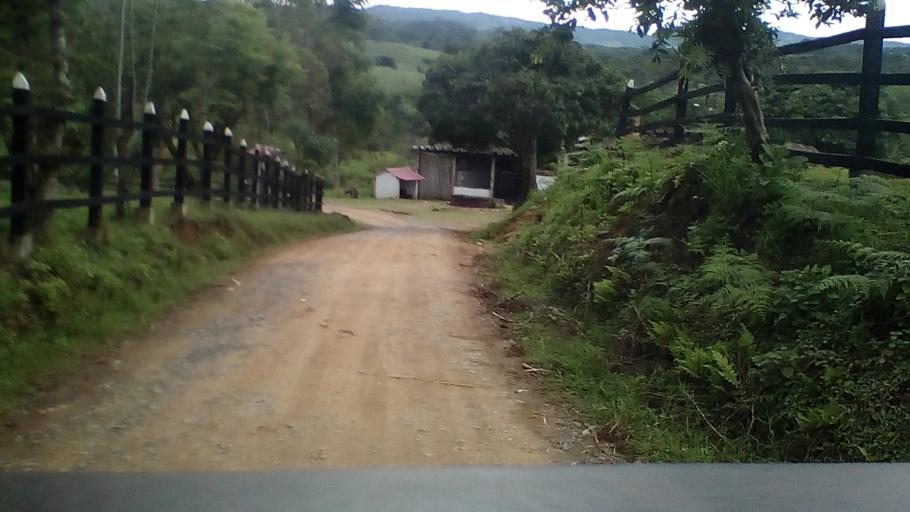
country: CO
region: Boyaca
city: Santana
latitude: 6.0199
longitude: -73.5138
